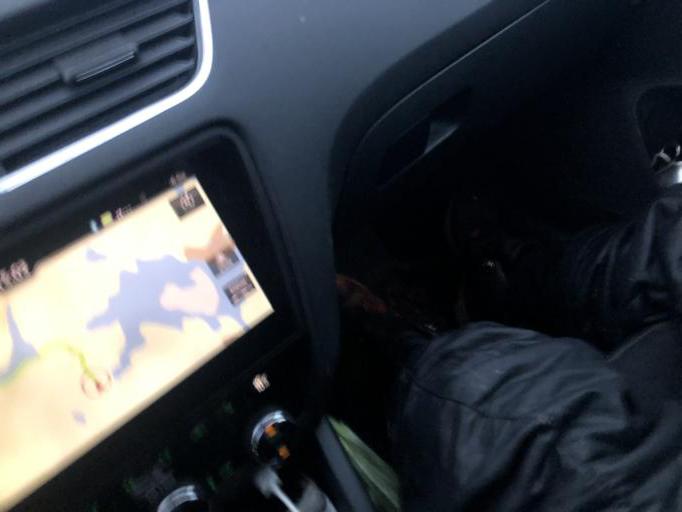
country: SE
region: Vaesternorrland
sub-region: Kramfors Kommun
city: Nordingra
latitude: 62.9118
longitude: 18.2352
